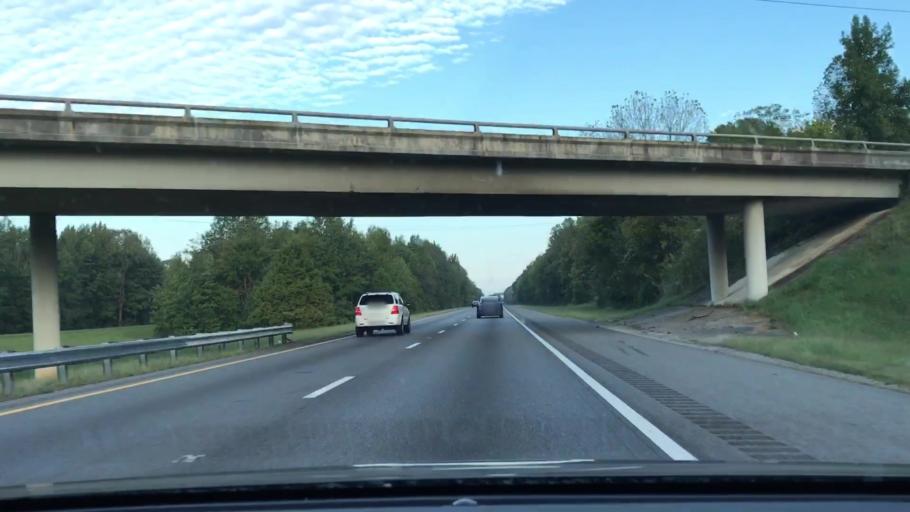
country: US
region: Kentucky
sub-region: Todd County
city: Guthrie
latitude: 36.4968
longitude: -87.1764
